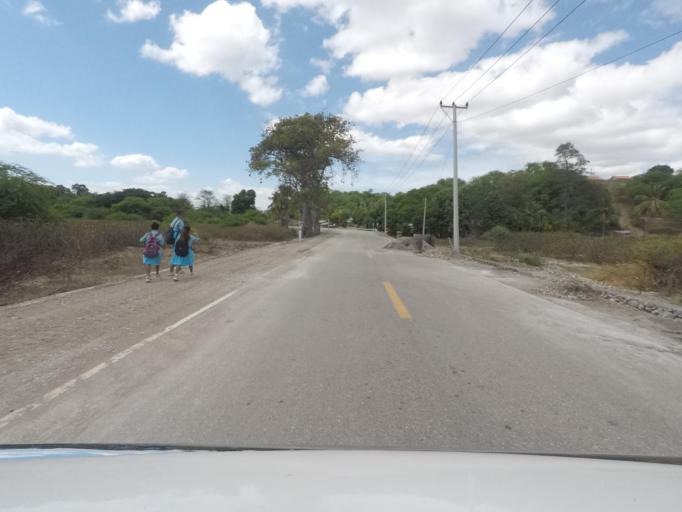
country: TL
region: Baucau
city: Baucau
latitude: -8.4104
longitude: 126.7366
